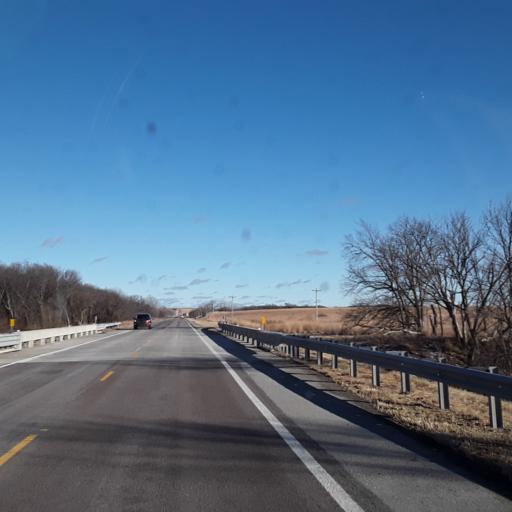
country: US
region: Kansas
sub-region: Cloud County
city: Concordia
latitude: 39.4962
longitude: -97.7414
